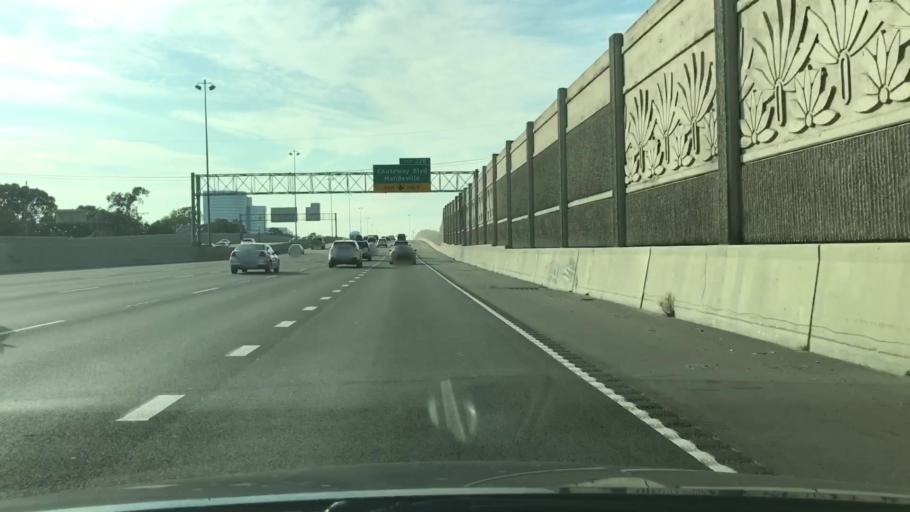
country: US
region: Louisiana
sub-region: Jefferson Parish
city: Metairie
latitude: 29.9971
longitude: -90.1393
